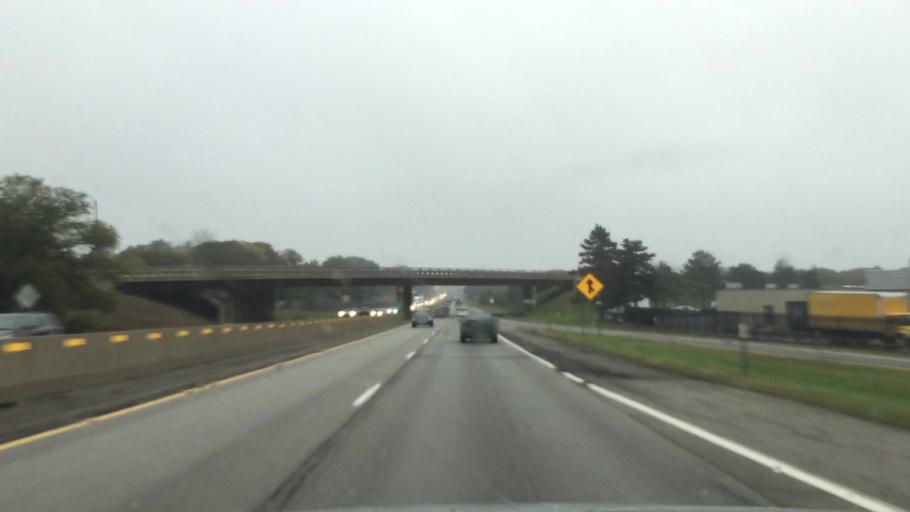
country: US
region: Michigan
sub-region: Kalamazoo County
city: Portage
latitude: 42.2458
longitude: -85.5580
